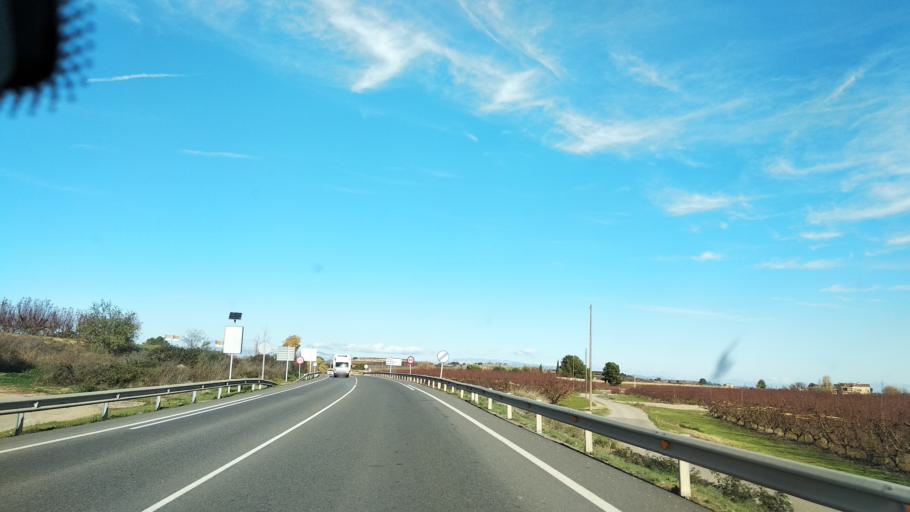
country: ES
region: Catalonia
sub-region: Provincia de Lleida
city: Alcoletge
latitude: 41.6613
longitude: 0.6627
